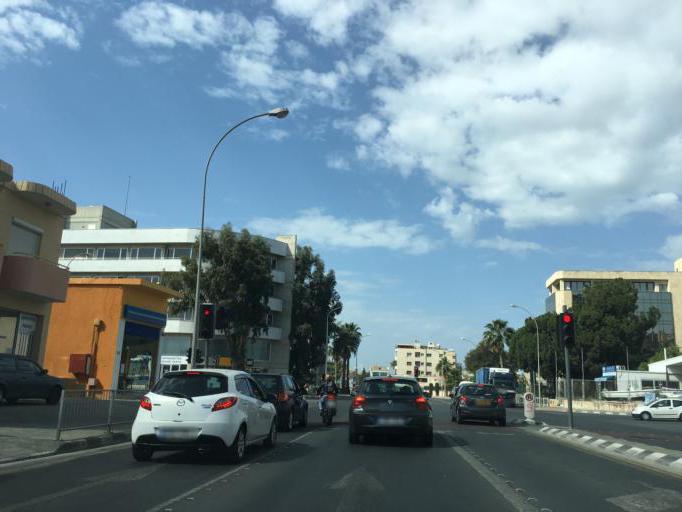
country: CY
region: Limassol
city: Limassol
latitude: 34.6673
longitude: 33.0254
